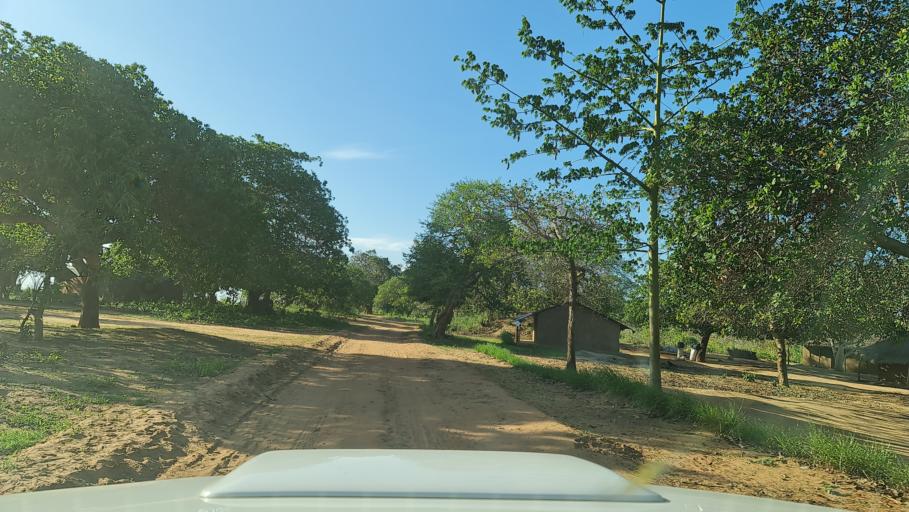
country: MZ
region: Nampula
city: Nacala
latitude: -14.7107
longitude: 40.3350
